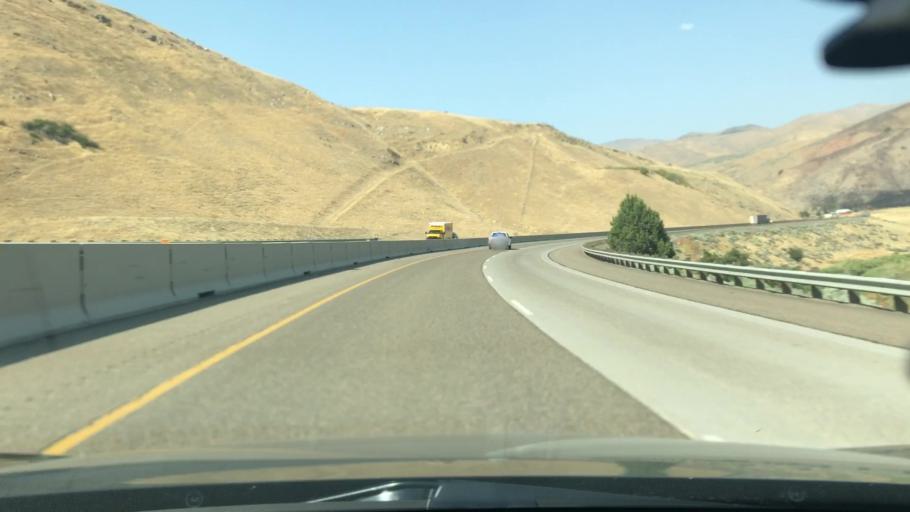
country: US
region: Idaho
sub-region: Washington County
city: Weiser
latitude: 44.4071
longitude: -117.3131
